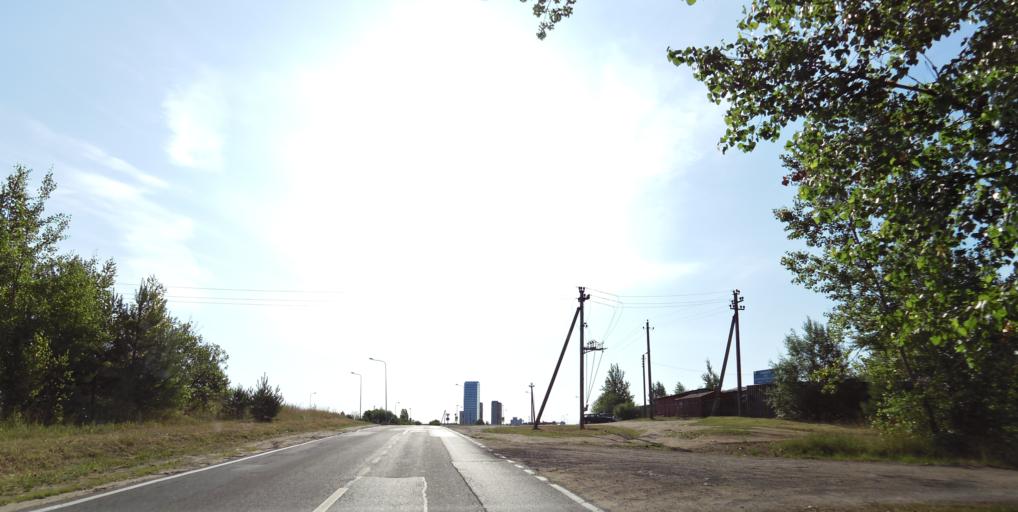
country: LT
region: Vilnius County
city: Pilaite
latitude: 54.7040
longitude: 25.1988
